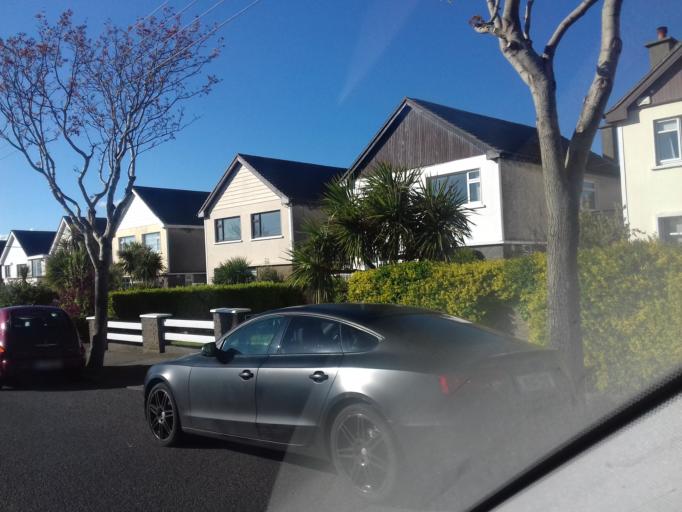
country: IE
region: Leinster
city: Sutton
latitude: 53.3768
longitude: -6.0983
